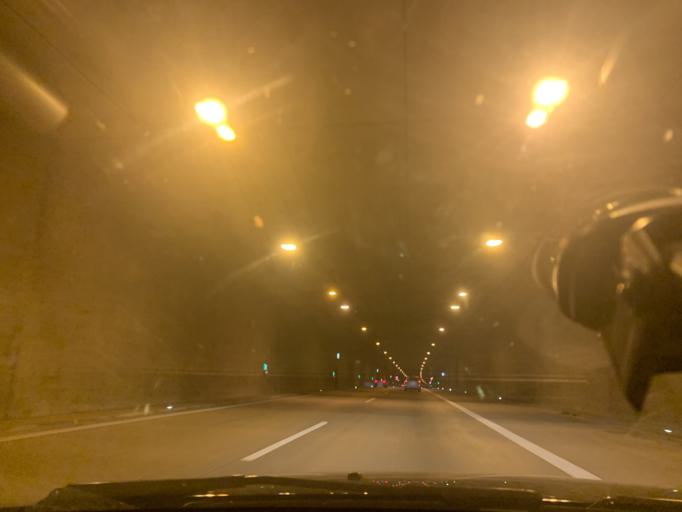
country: DE
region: Bavaria
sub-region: Upper Bavaria
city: Germering
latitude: 48.1590
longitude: 11.4035
